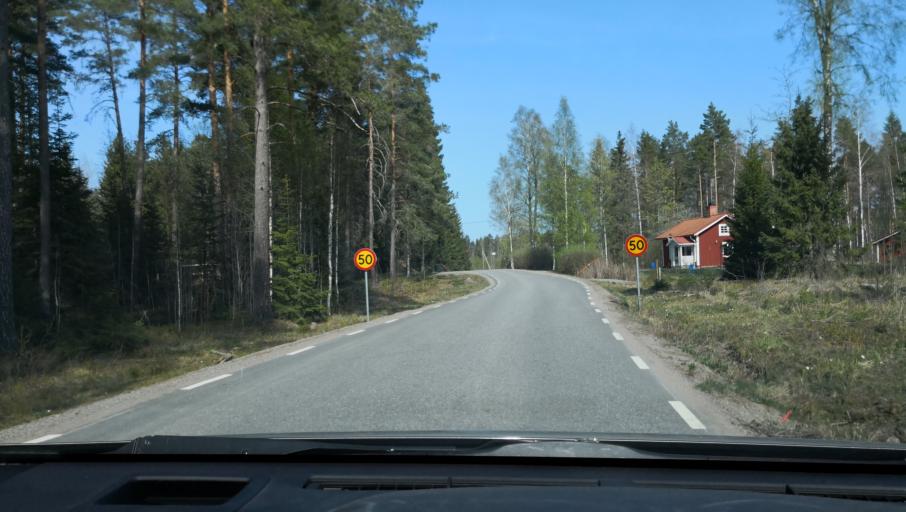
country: SE
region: Vaestmanland
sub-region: Sala Kommun
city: Sala
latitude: 60.0037
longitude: 16.6699
